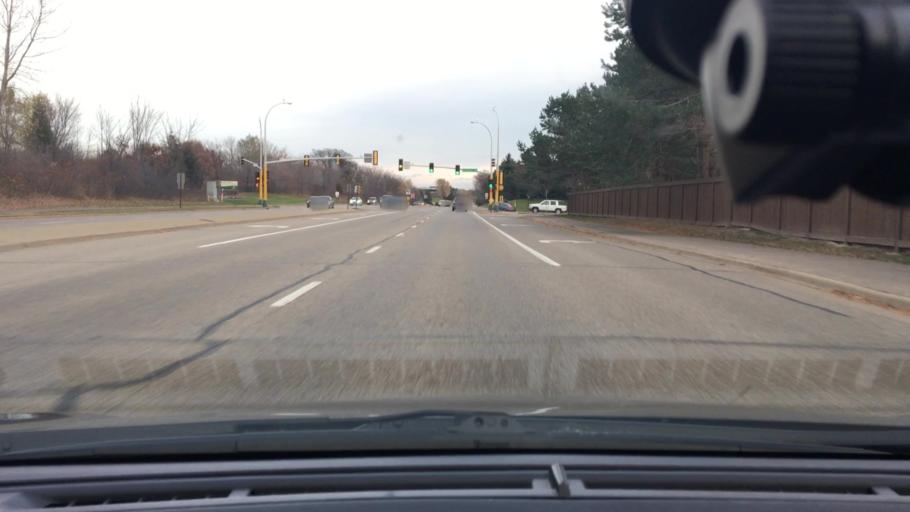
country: US
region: Minnesota
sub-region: Hennepin County
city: Maple Grove
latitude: 45.0584
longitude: -93.4220
